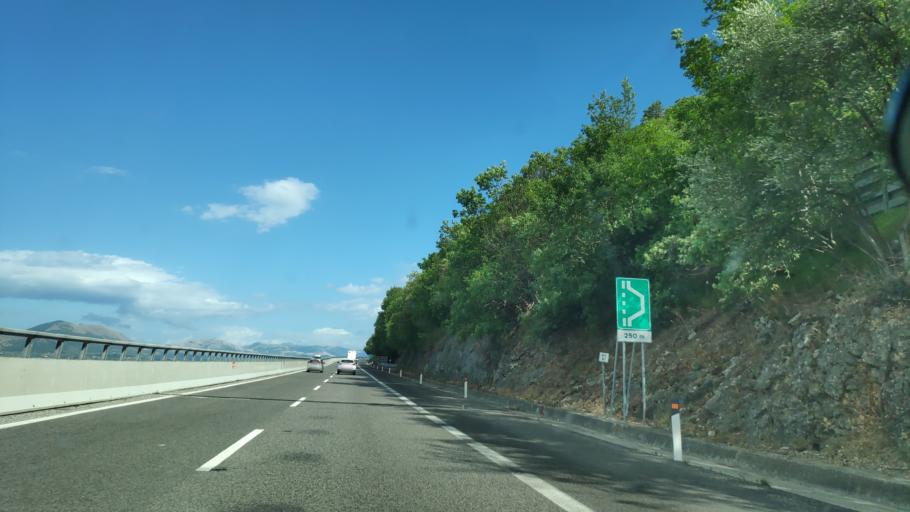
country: IT
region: Campania
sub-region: Provincia di Salerno
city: Sicignano degli Alburni
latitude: 40.5916
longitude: 15.3276
